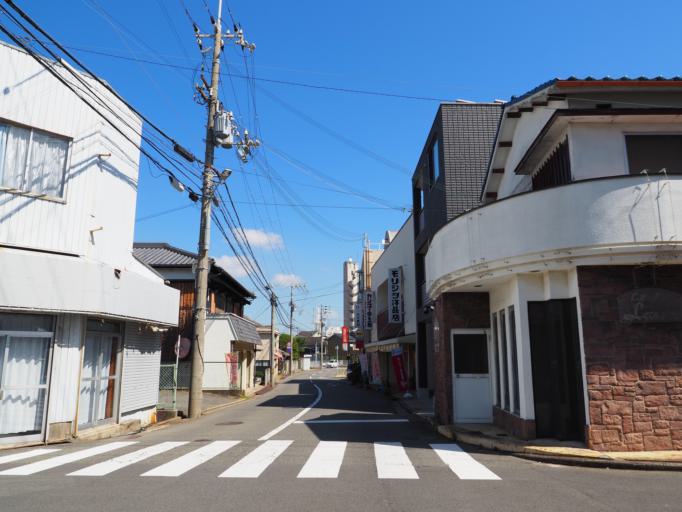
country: JP
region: Hyogo
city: Tatsunocho-tominaga
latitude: 34.7827
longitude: 134.5886
